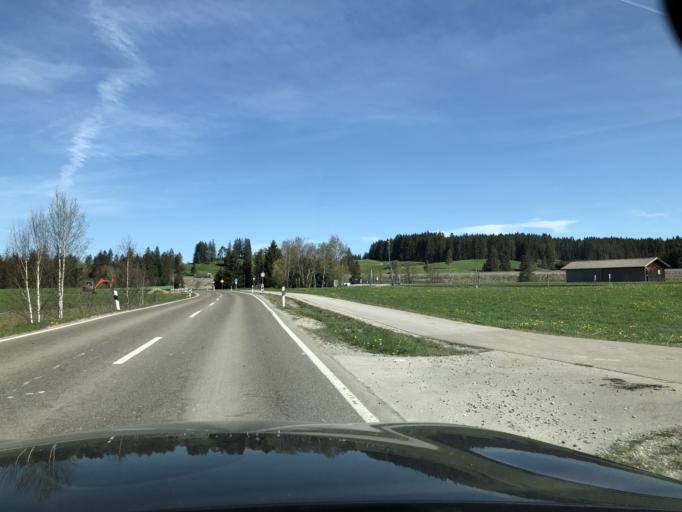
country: DE
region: Bavaria
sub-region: Swabia
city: Eisenberg
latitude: 47.6248
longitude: 10.6060
